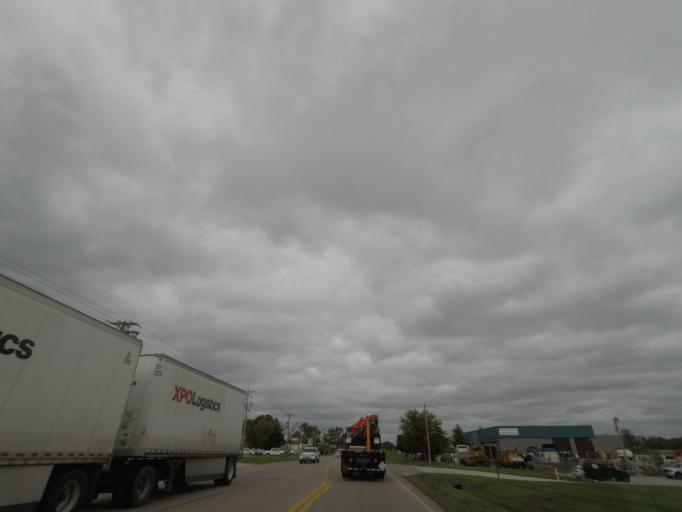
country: US
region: Iowa
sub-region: Polk County
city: Saylorville
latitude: 41.6591
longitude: -93.6005
